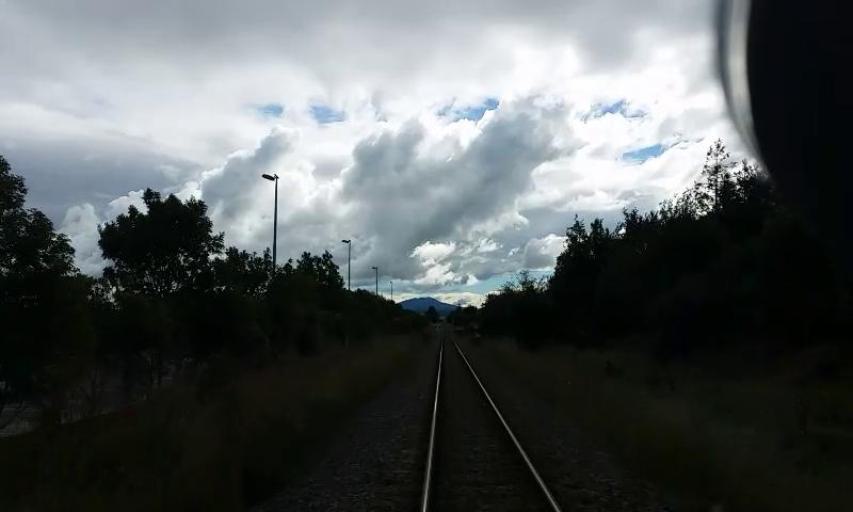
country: NZ
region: Canterbury
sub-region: Waimakariri District
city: Woodend
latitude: -43.3126
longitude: 172.6005
